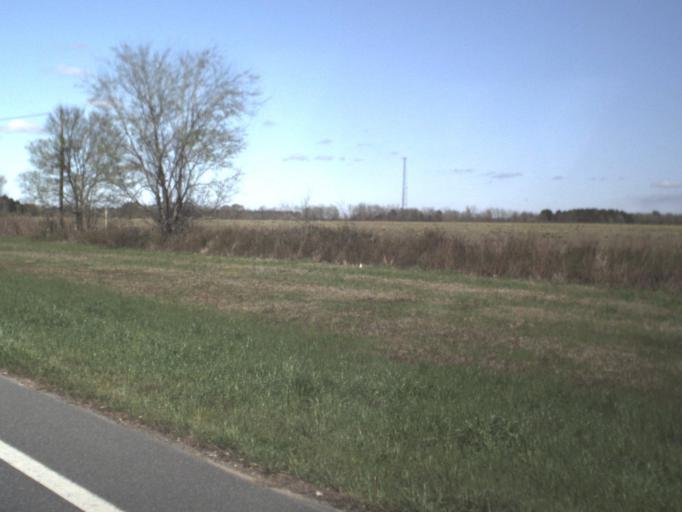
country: US
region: Florida
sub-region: Gadsden County
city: Gretna
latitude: 30.6344
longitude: -84.6730
